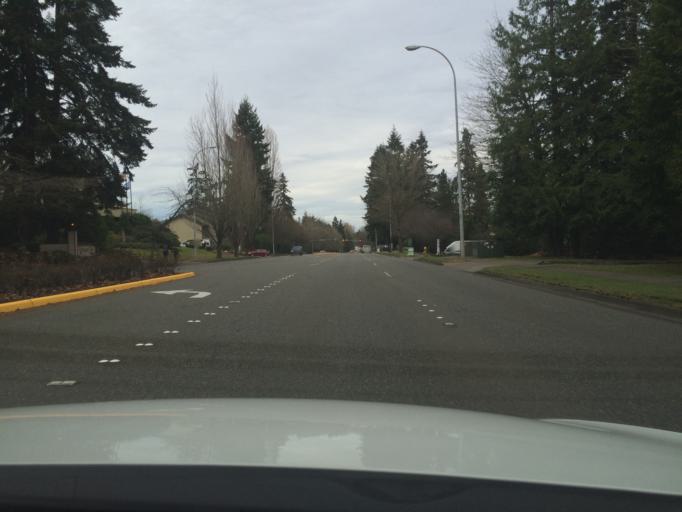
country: US
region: Washington
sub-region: King County
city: Redmond
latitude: 47.6502
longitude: -122.1431
